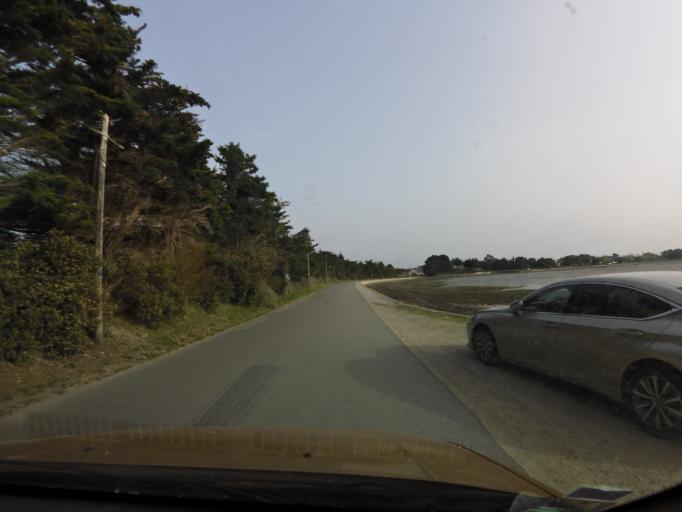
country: FR
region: Brittany
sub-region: Departement du Morbihan
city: Sene
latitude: 47.5821
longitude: -2.7156
